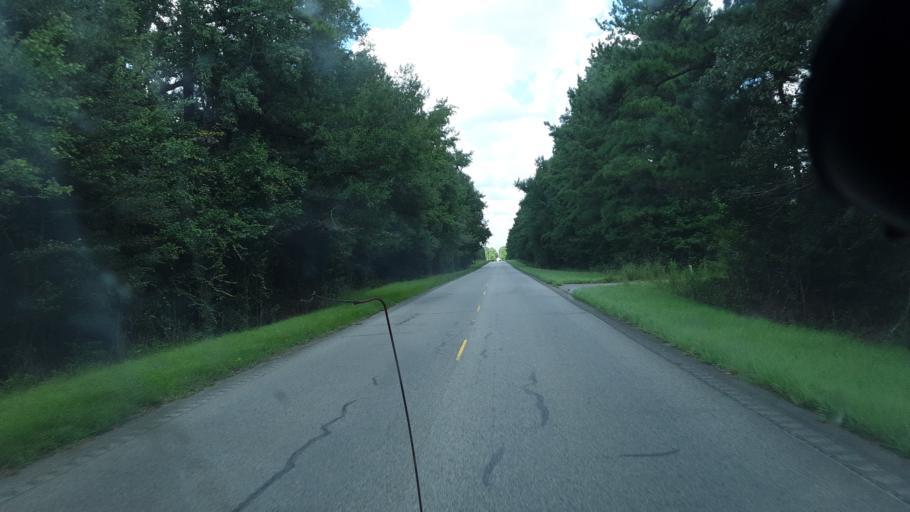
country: US
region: South Carolina
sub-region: Williamsburg County
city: Andrews
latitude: 33.5771
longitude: -79.4491
